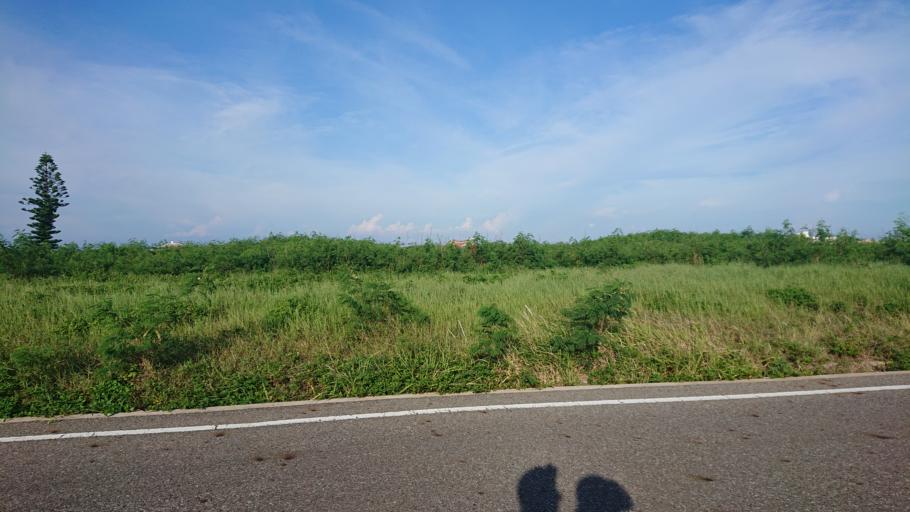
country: TW
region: Taiwan
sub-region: Penghu
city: Ma-kung
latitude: 23.6040
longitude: 119.5170
